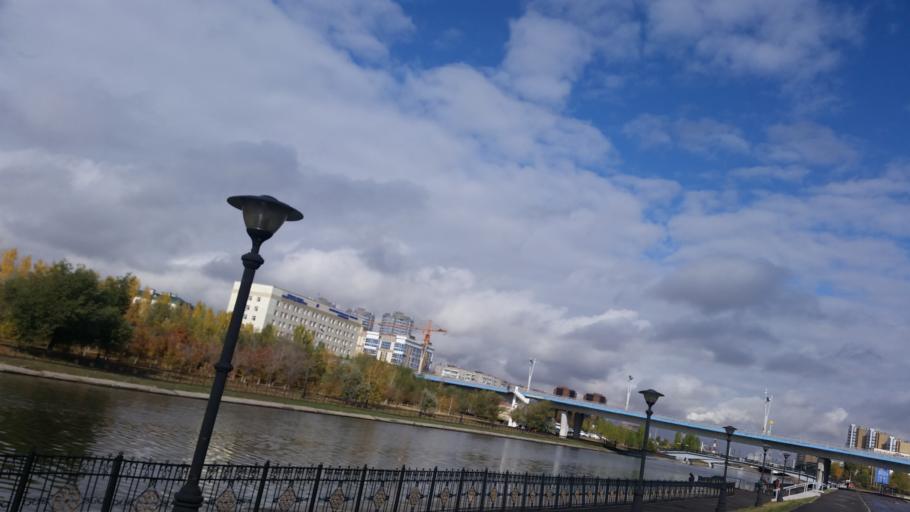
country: KZ
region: Astana Qalasy
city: Astana
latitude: 51.1571
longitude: 71.4638
